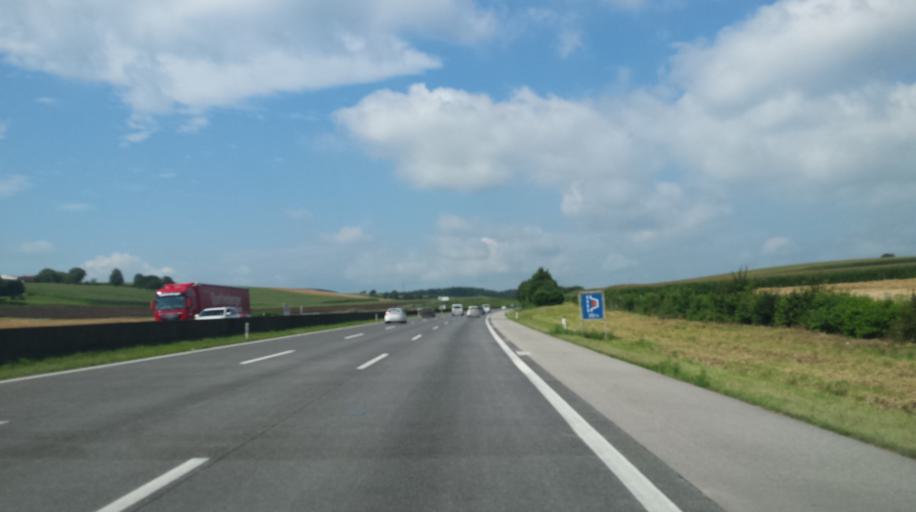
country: AT
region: Lower Austria
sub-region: Politischer Bezirk Melk
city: Petzenkirchen
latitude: 48.1639
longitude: 15.1549
